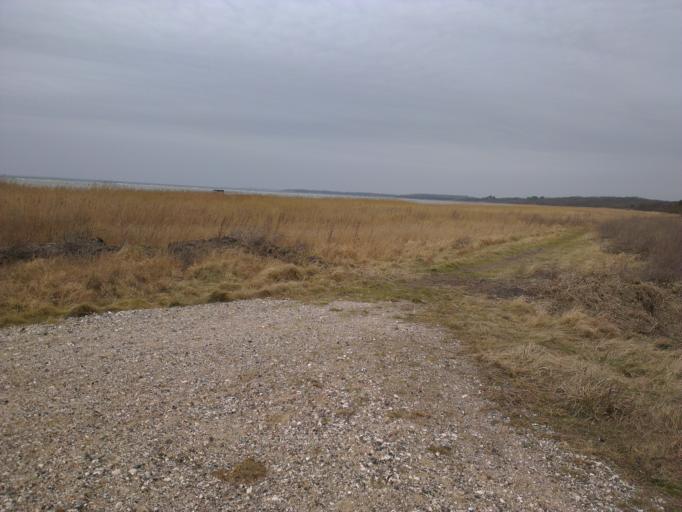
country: DK
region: Capital Region
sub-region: Frederikssund Kommune
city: Jaegerspris
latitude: 55.8429
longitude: 11.9583
